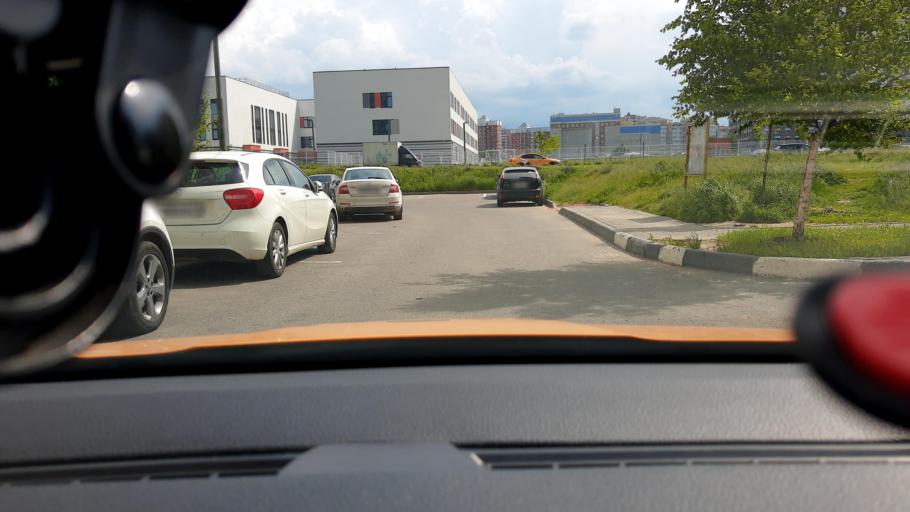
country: RU
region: Moscow
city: Khimki
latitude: 55.9064
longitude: 37.3952
